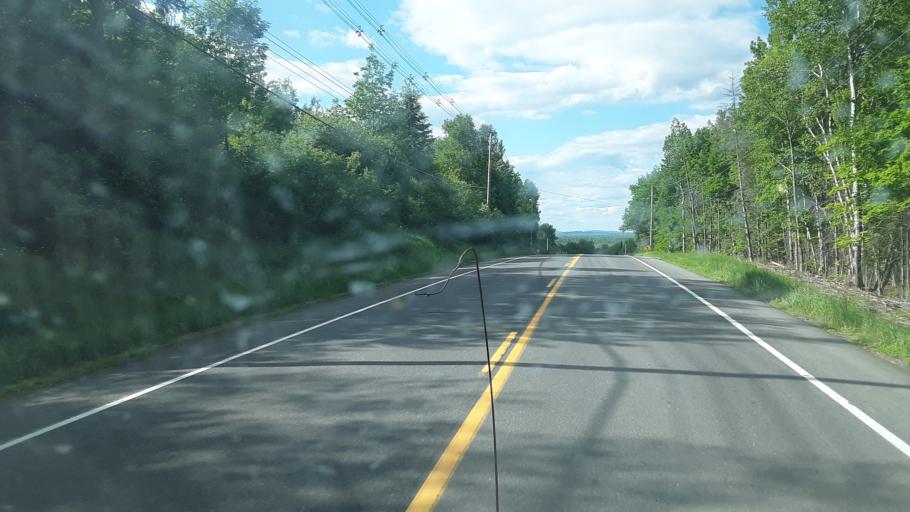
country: US
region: Maine
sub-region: Penobscot County
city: Patten
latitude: 45.8811
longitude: -68.4179
